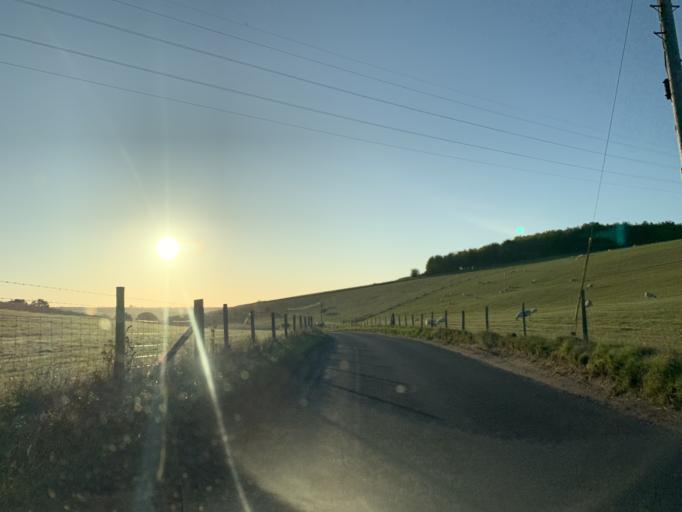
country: GB
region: England
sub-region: Wiltshire
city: Woodford
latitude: 51.1244
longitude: -1.8392
